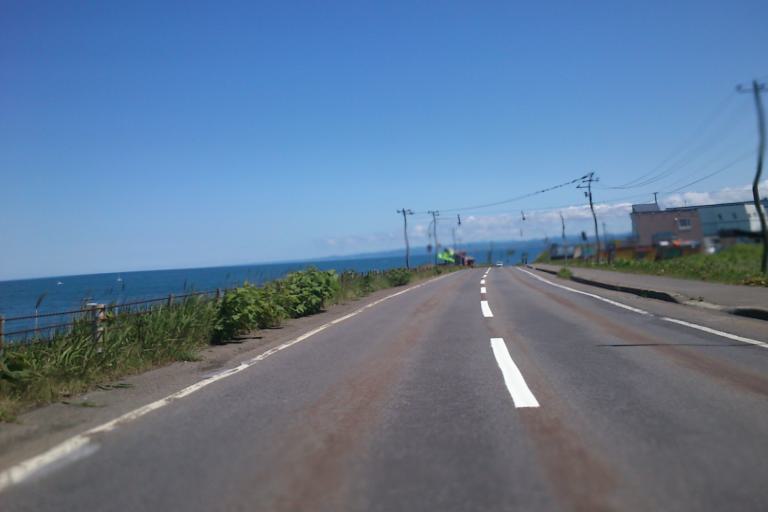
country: JP
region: Hokkaido
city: Rumoi
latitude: 43.8515
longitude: 141.5071
